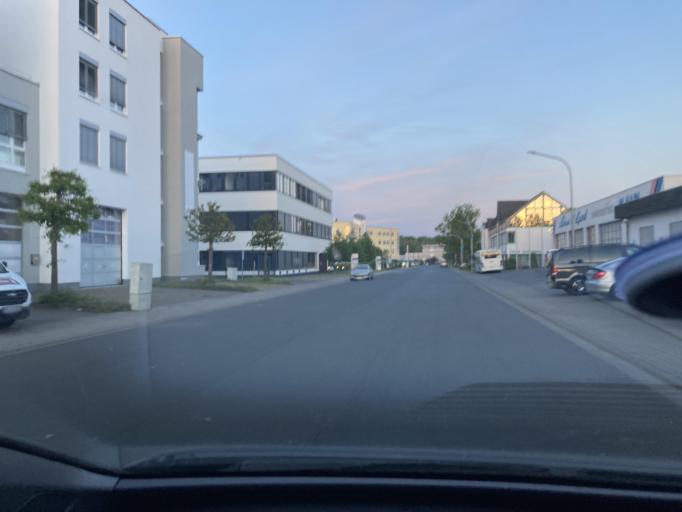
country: DE
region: Hesse
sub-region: Regierungsbezirk Darmstadt
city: Eppertshausen
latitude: 49.9667
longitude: 8.8171
